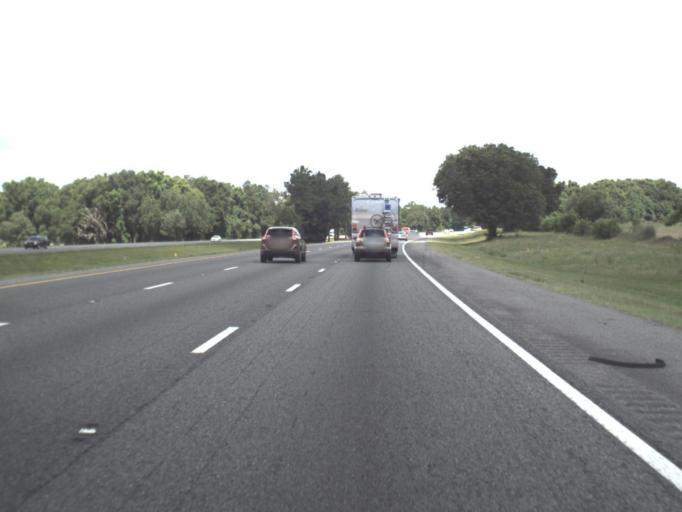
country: US
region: Florida
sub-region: Suwannee County
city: Wellborn
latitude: 30.2384
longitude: -82.7366
